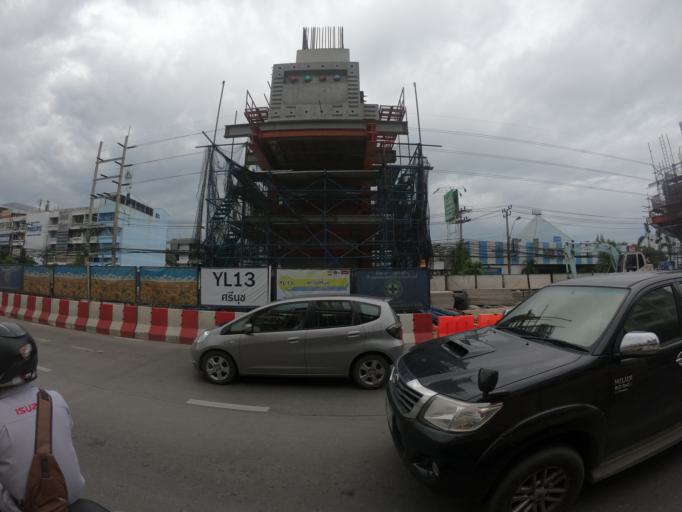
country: TH
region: Bangkok
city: Suan Luang
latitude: 13.7115
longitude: 100.6439
